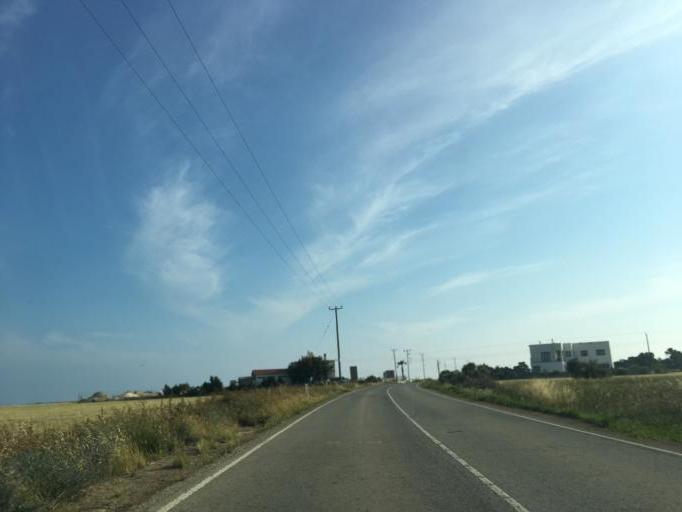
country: CY
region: Larnaka
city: Tersefanou
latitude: 34.7883
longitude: 33.4825
